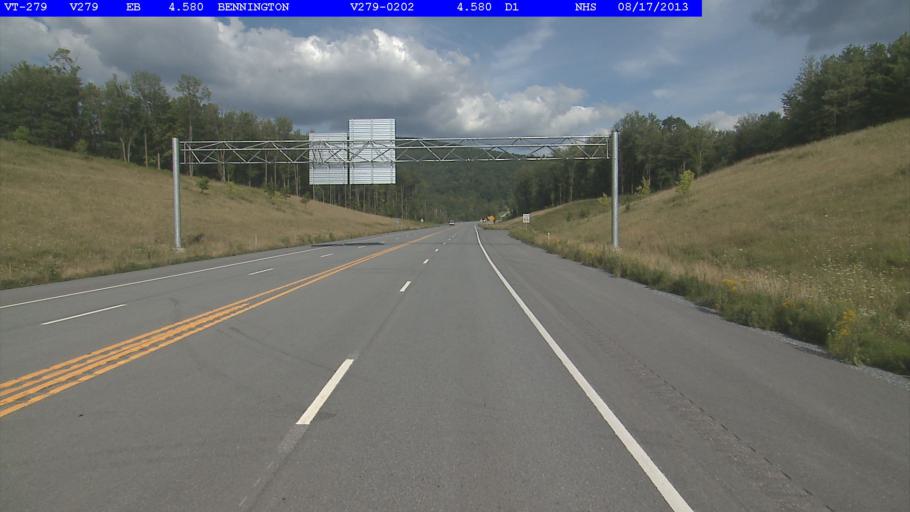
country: US
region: Vermont
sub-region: Bennington County
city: Bennington
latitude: 42.9017
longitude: -73.1881
